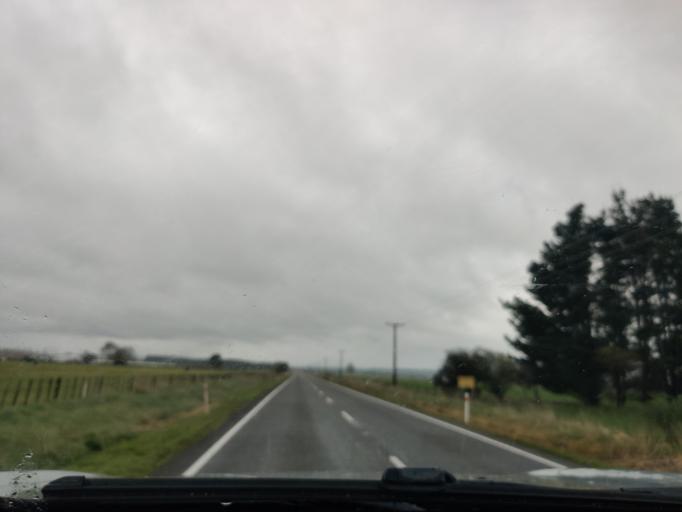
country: NZ
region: Hawke's Bay
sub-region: Hastings District
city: Hastings
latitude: -40.0128
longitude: 176.3683
